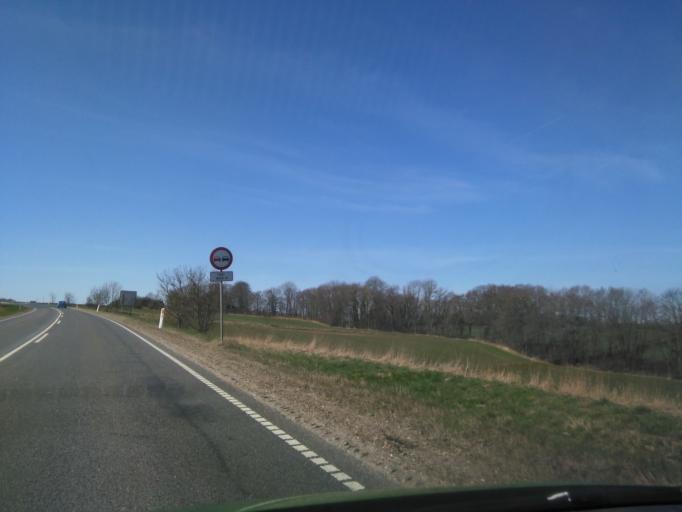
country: DK
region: Central Jutland
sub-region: Skanderborg Kommune
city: Ry
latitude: 56.0232
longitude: 9.8260
